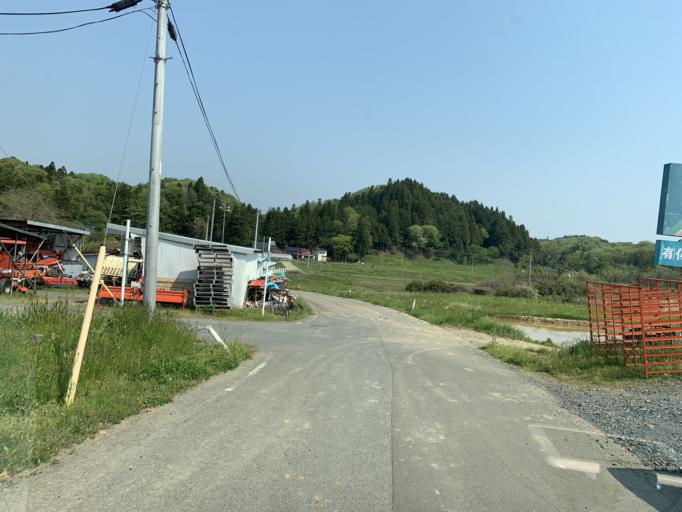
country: JP
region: Iwate
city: Ichinoseki
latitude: 38.8602
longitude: 141.0572
